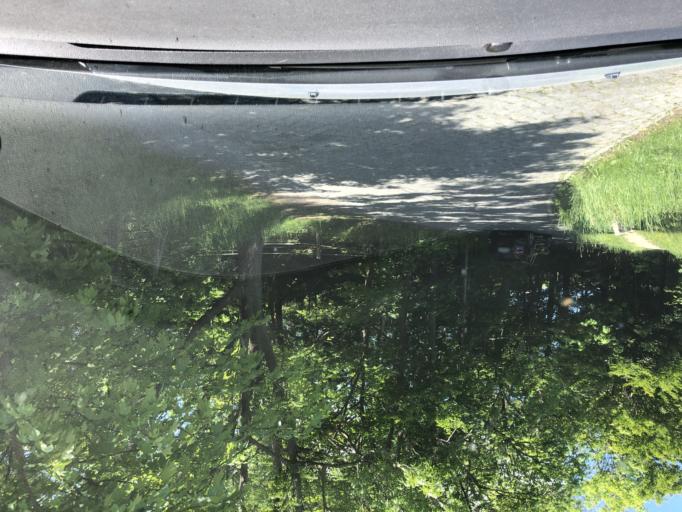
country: DE
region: Saxony
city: Radebeul
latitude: 51.0583
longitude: 13.6440
